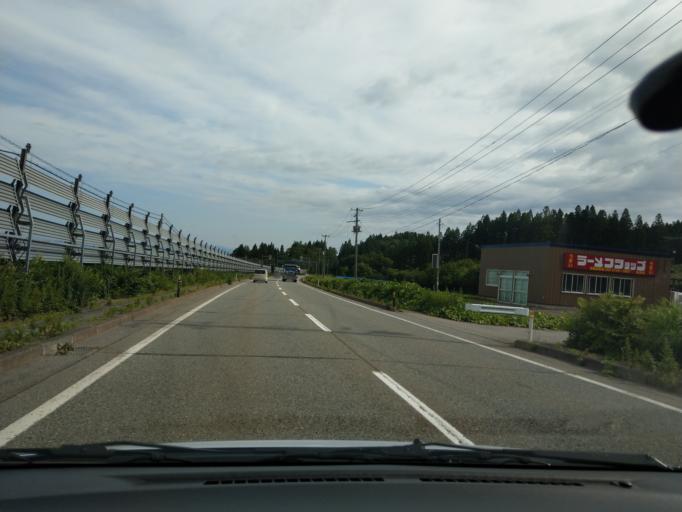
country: JP
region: Akita
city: Yokotemachi
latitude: 39.3848
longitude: 140.5678
